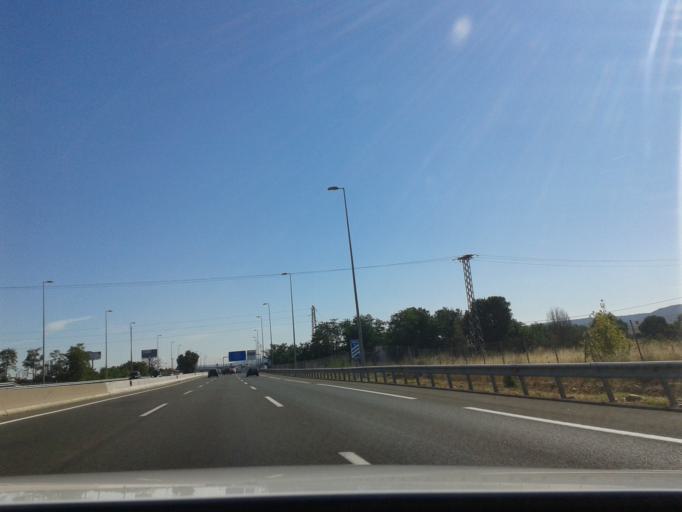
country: ES
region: Madrid
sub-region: Provincia de Madrid
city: Meco
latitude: 40.5262
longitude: -3.2973
